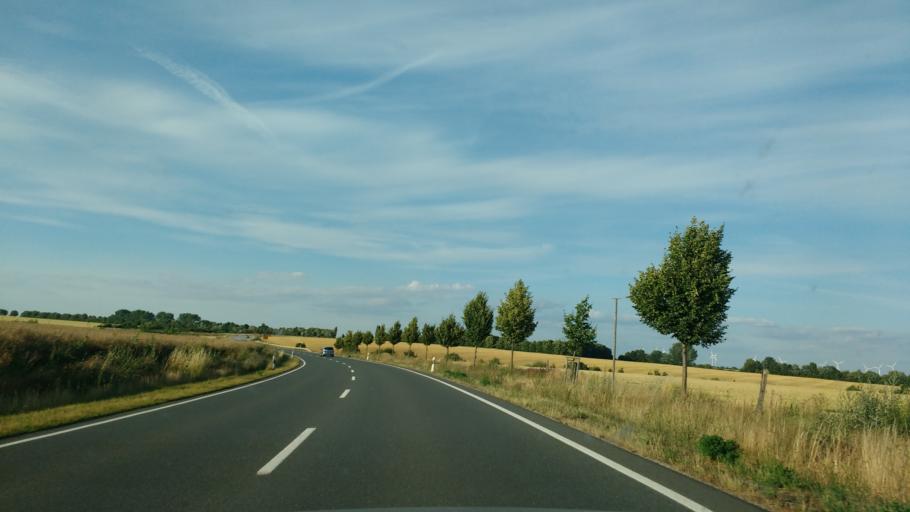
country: DE
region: Saxony-Anhalt
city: Querfurt
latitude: 51.4008
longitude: 11.6274
